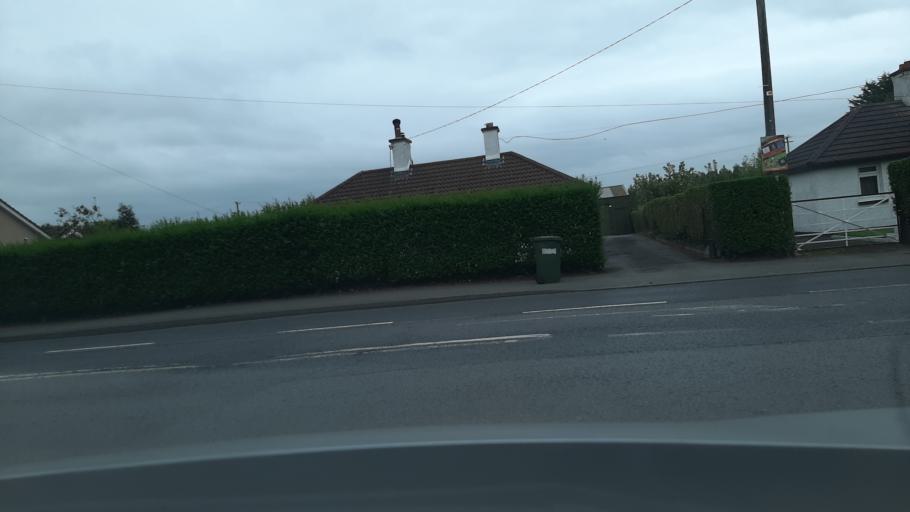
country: IE
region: Leinster
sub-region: Kildare
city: Kildare
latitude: 53.1549
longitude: -6.8927
